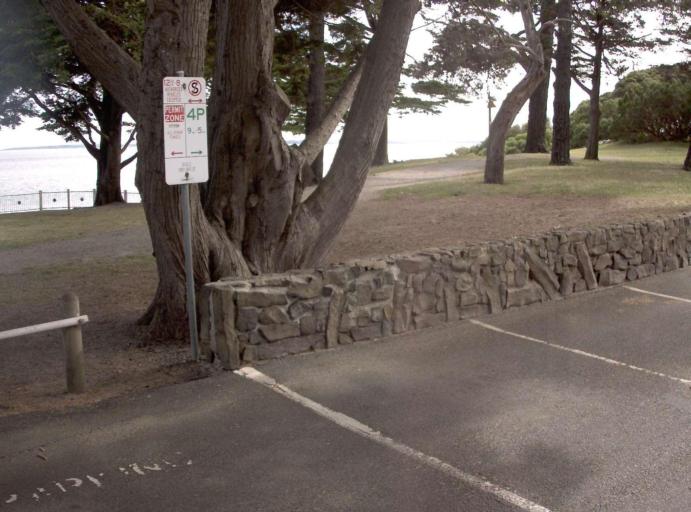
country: AU
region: Victoria
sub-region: Bass Coast
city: Cowes
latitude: -38.4480
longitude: 145.2422
